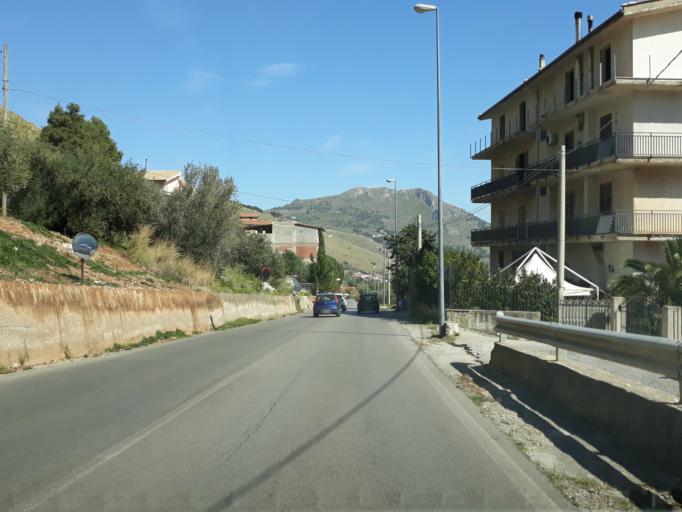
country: IT
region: Sicily
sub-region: Palermo
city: Belmonte Mezzagno
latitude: 38.0490
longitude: 13.4048
